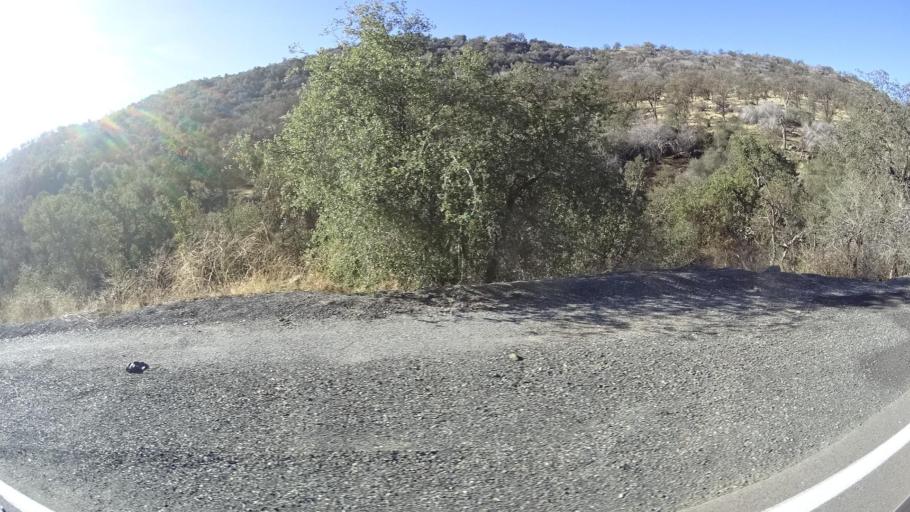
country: US
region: California
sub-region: Kern County
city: Alta Sierra
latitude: 35.7075
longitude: -118.7752
